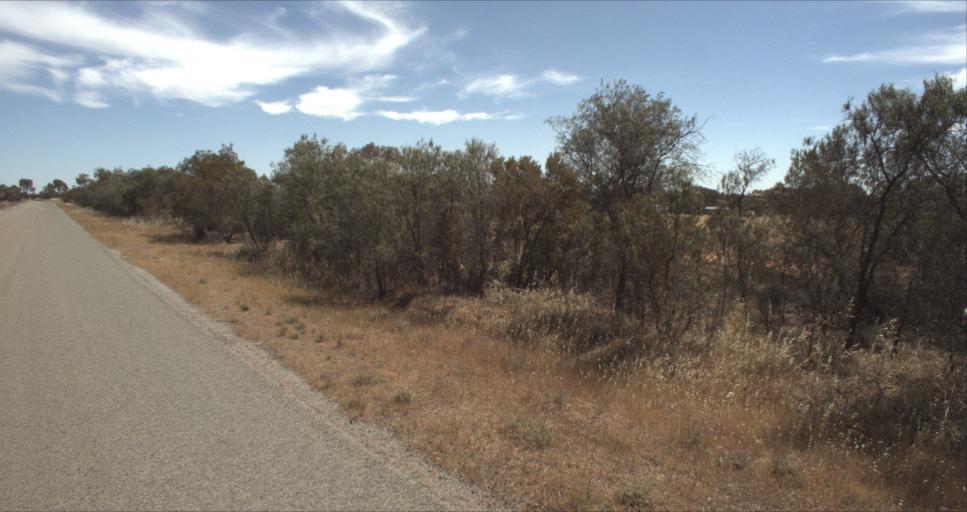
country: AU
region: New South Wales
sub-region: Leeton
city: Leeton
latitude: -34.5807
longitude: 146.4313
